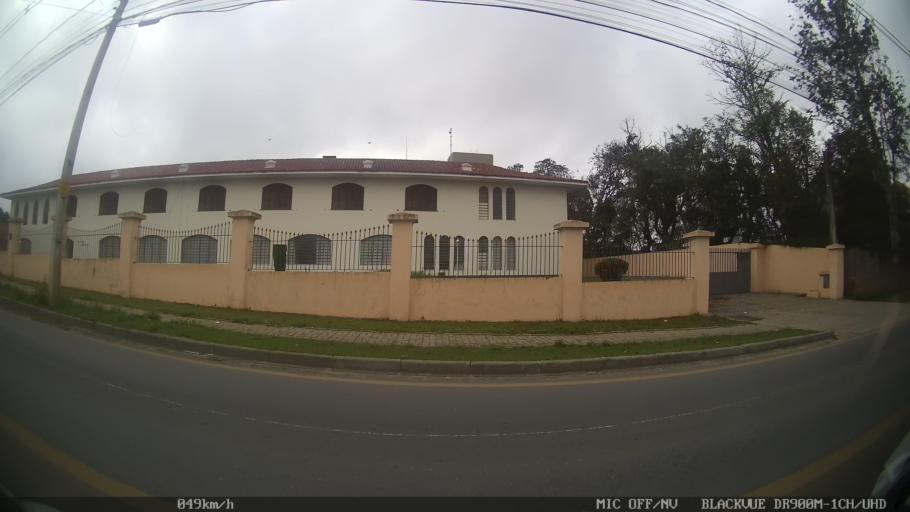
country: BR
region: Parana
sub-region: Almirante Tamandare
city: Almirante Tamandare
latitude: -25.3648
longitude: -49.2717
